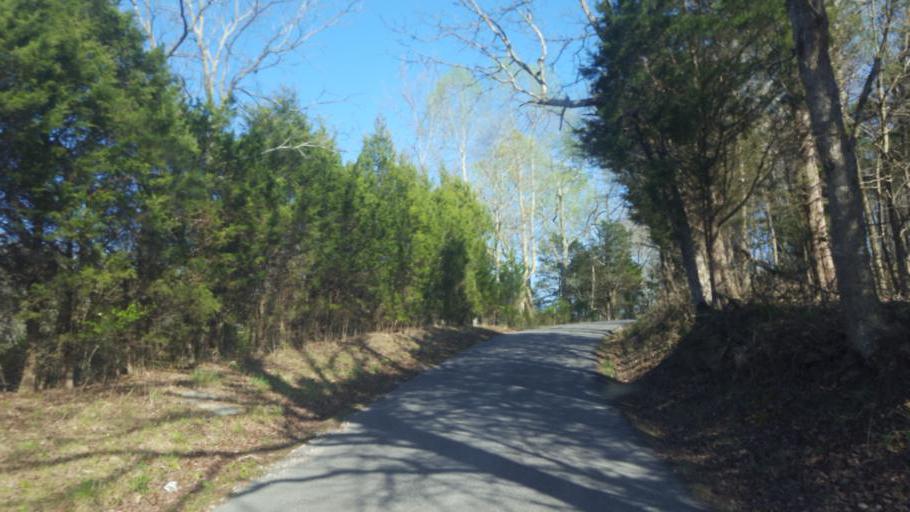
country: US
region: Kentucky
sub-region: Barren County
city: Cave City
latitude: 37.2036
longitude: -86.0219
